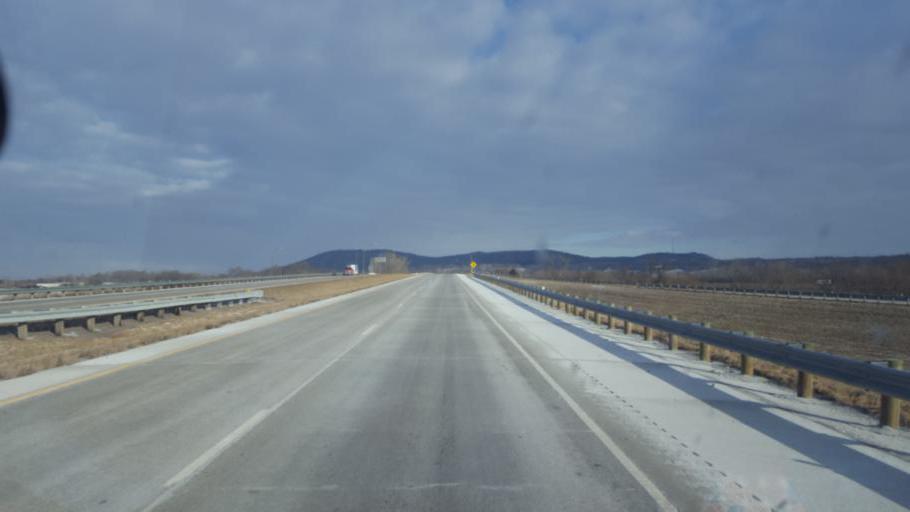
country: US
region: Ohio
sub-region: Ross County
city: Chillicothe
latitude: 39.3149
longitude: -82.9393
